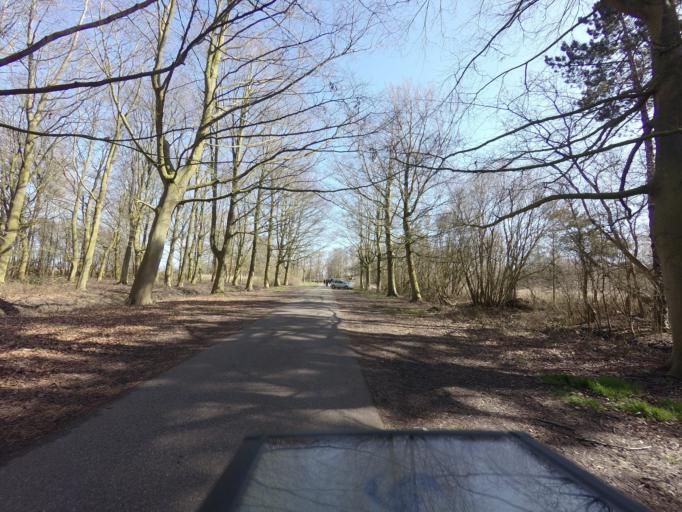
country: NL
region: Zeeland
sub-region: Schouwen-Duiveland
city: Renesse
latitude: 51.7348
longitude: 3.7840
